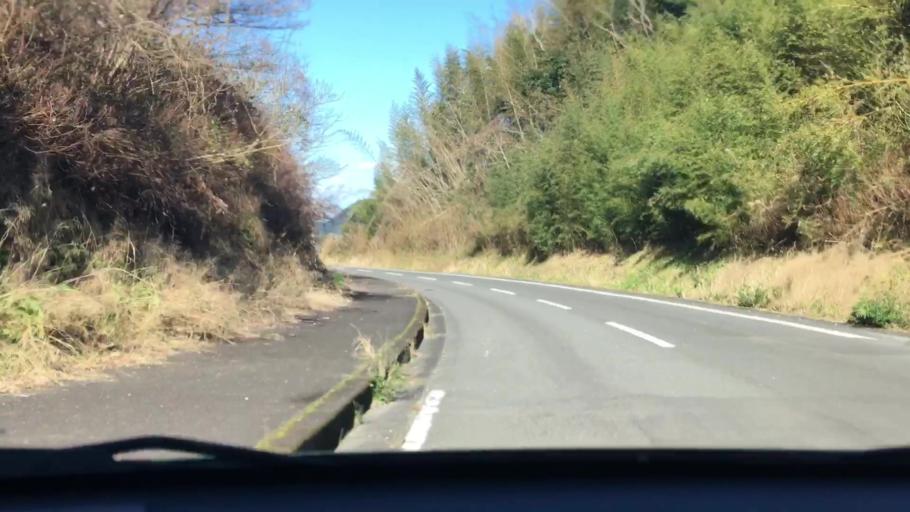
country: JP
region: Kagoshima
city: Satsumasendai
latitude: 31.7690
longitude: 130.4016
